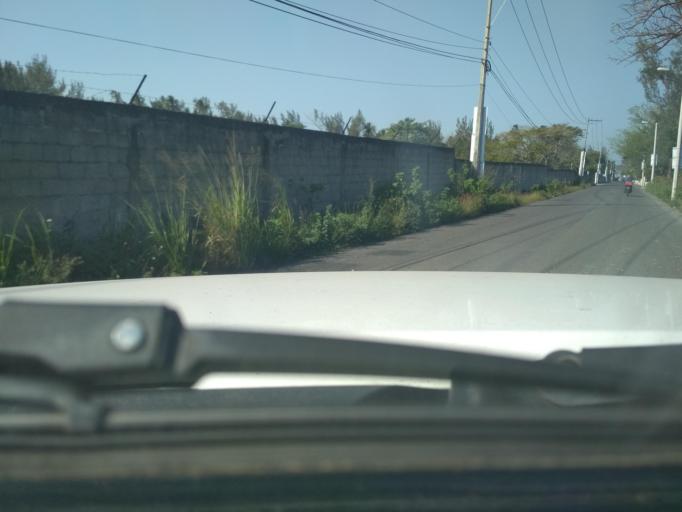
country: MX
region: Veracruz
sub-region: Veracruz
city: Las Amapolas
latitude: 19.1515
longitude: -96.2104
